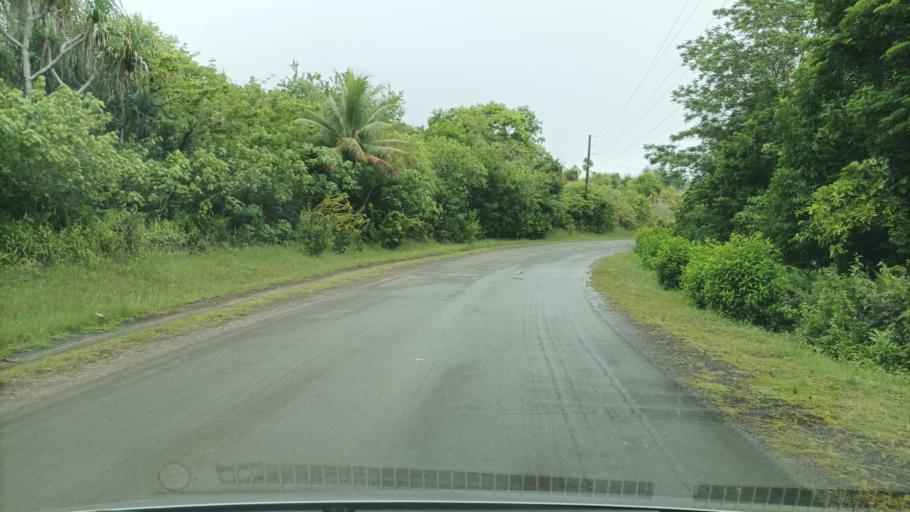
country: FM
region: Yap
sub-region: Weloy Municipality
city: Colonia
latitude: 9.5480
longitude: 138.1571
